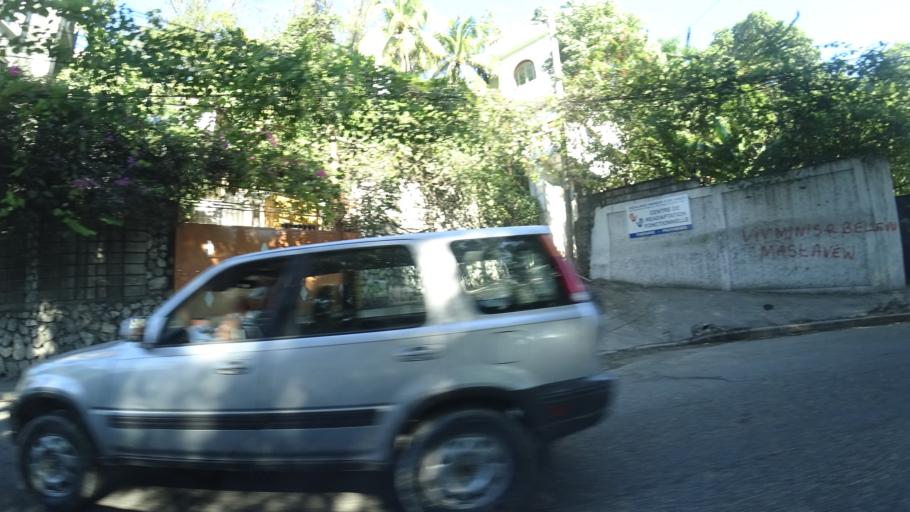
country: HT
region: Ouest
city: Delmas 73
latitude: 18.5348
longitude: -72.3125
